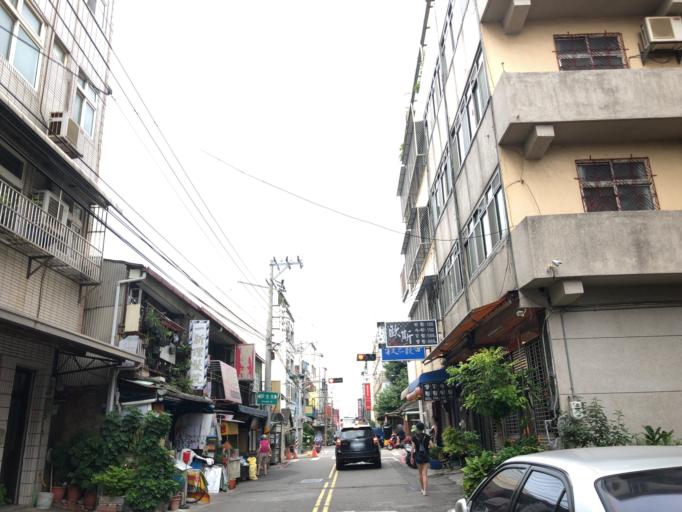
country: TW
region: Taiwan
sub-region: Taichung City
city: Taichung
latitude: 24.2383
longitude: 120.5623
